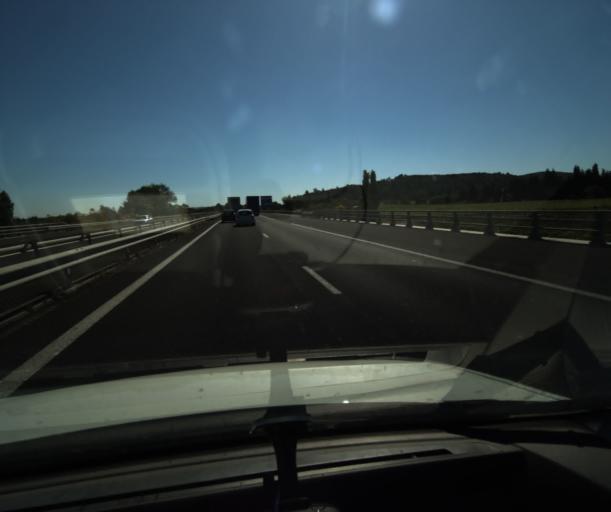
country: FR
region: Languedoc-Roussillon
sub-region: Departement de l'Aude
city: Ferrals-les-Corbieres
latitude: 43.1701
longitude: 2.7507
